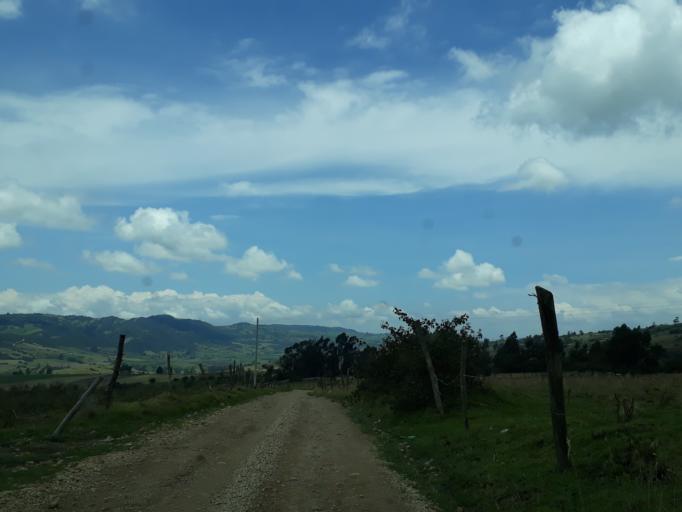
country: CO
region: Cundinamarca
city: Lenguazaque
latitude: 5.3164
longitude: -73.6273
